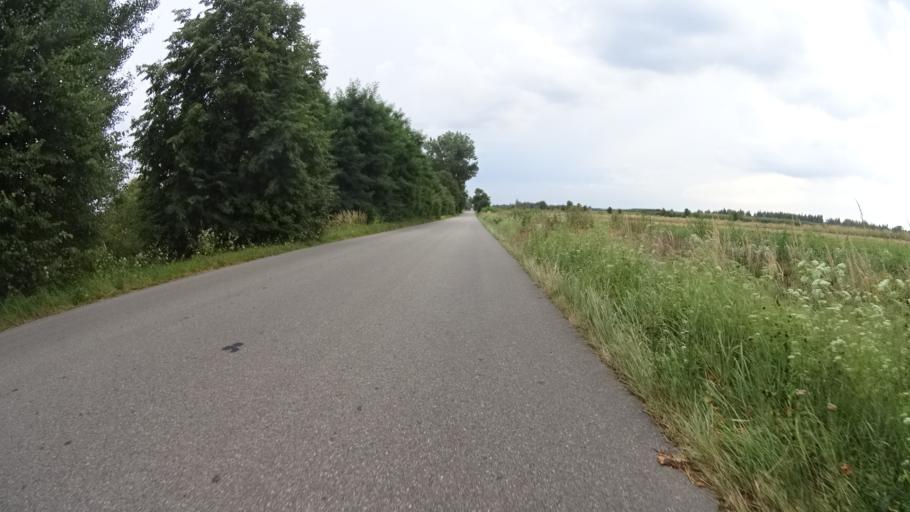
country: PL
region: Masovian Voivodeship
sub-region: Powiat grojecki
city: Goszczyn
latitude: 51.6775
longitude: 20.8593
